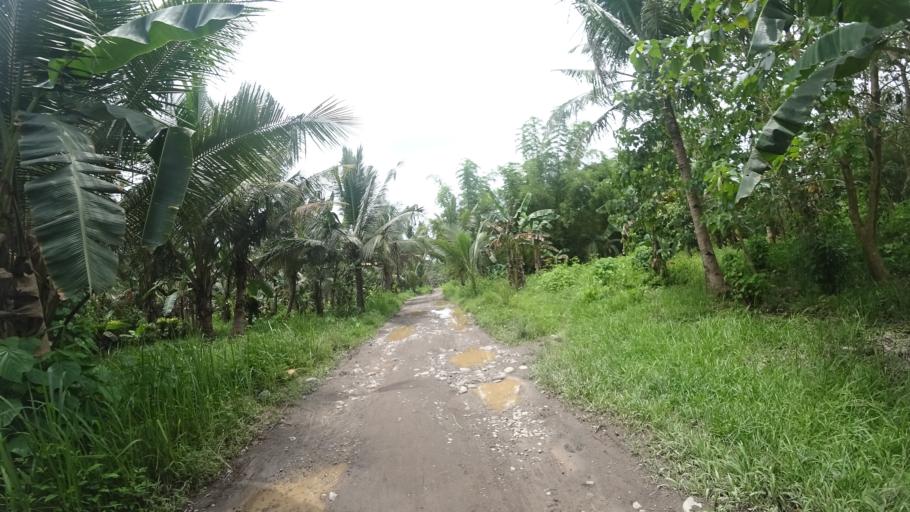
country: PH
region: Eastern Visayas
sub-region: Province of Leyte
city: Jaro
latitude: 11.2029
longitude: 124.8051
